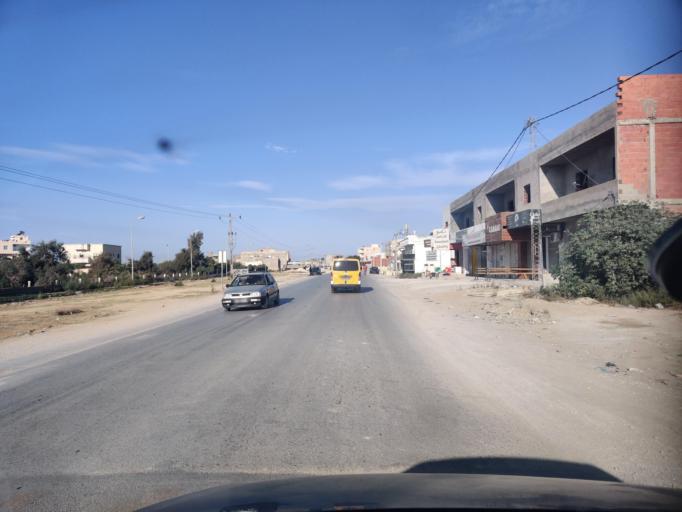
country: TN
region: Ariana
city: Ariana
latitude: 36.9567
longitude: 10.2086
